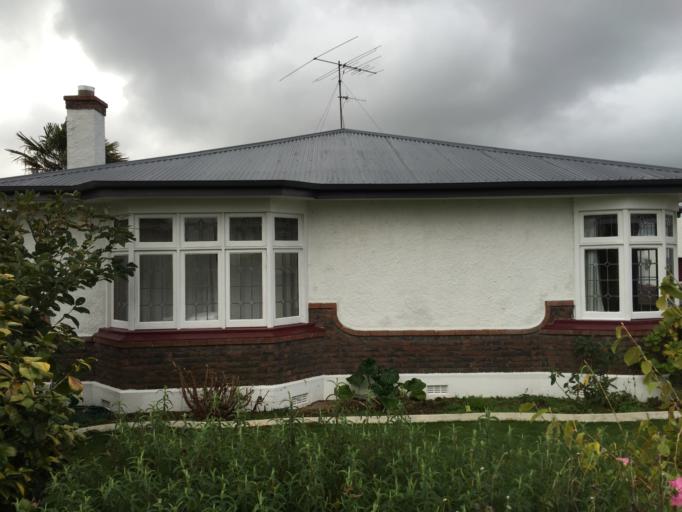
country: NZ
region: Southland
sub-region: Invercargill City
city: Invercargill
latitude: -46.4087
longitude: 168.3677
